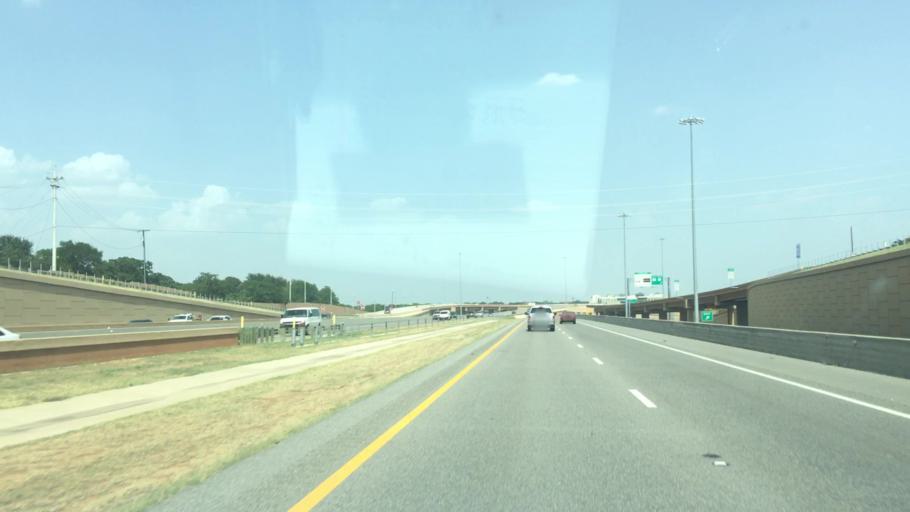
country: US
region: Texas
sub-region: Tarrant County
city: Bedford
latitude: 32.8400
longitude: -97.1589
